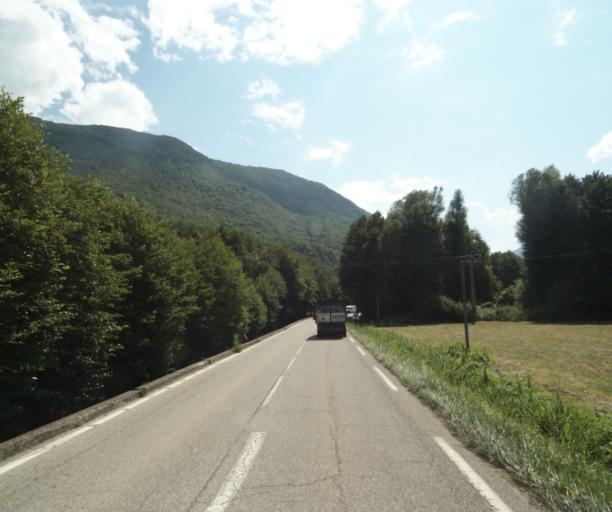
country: FR
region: Rhone-Alpes
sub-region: Departement de l'Isere
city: Vizille
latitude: 45.0855
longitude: 5.7891
